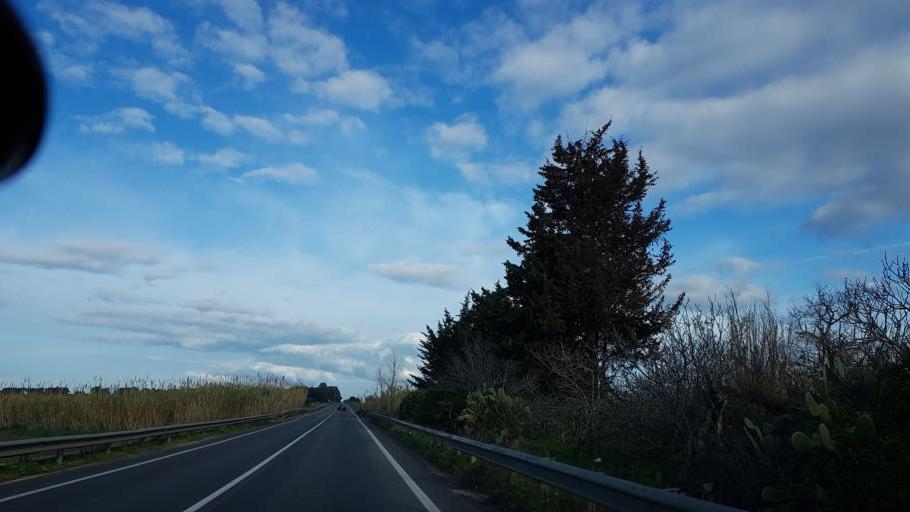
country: IT
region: Apulia
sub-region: Provincia di Brindisi
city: Tuturano
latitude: 40.5629
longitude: 17.9715
